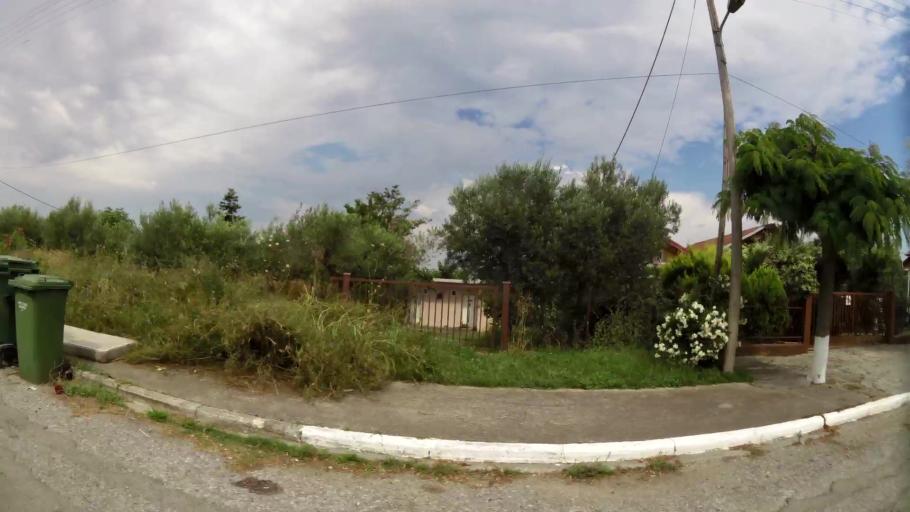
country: GR
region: Central Macedonia
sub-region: Nomos Pierias
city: Makrygialos
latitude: 40.4183
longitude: 22.6074
